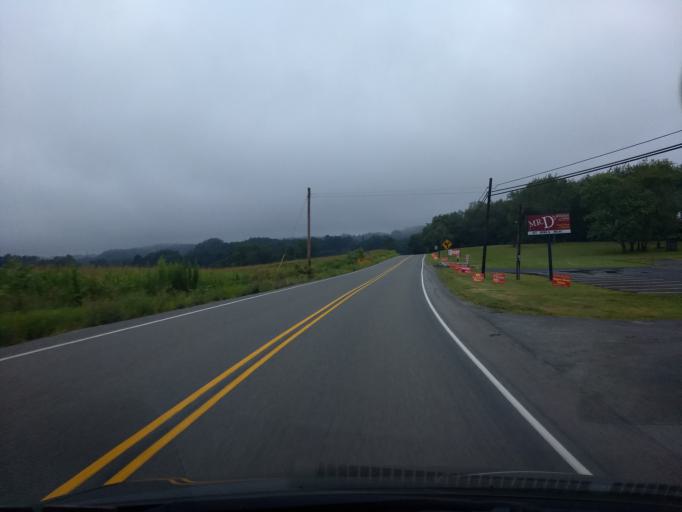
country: US
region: Pennsylvania
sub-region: Westmoreland County
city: Greensburg
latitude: 40.3427
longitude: -79.4962
